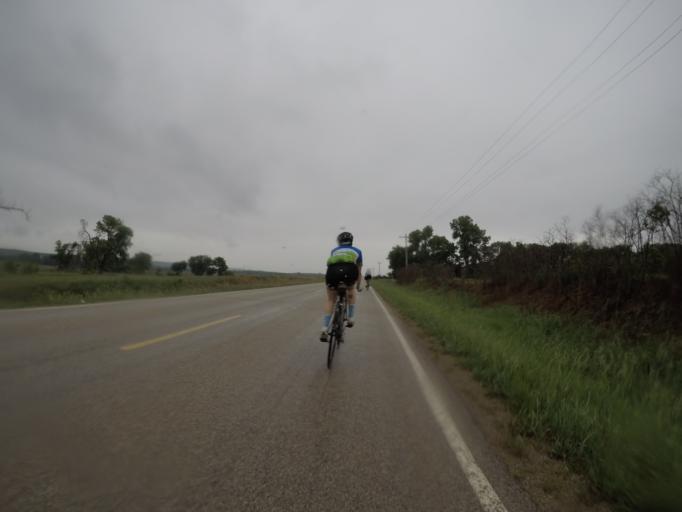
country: US
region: Kansas
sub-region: Pottawatomie County
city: Wamego
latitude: 39.3690
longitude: -96.2212
